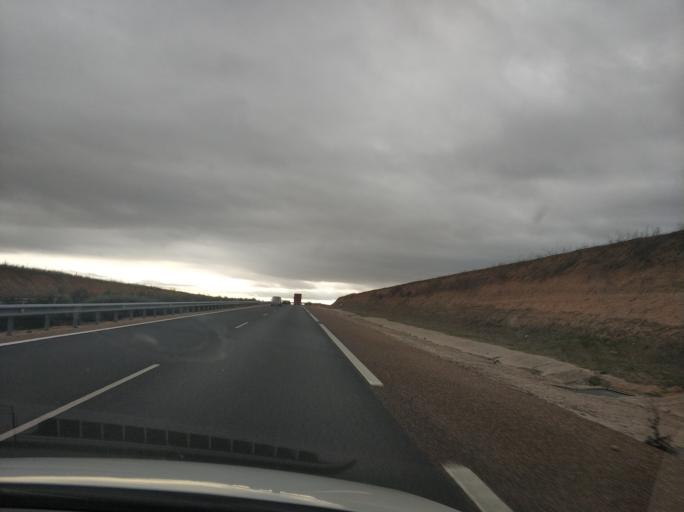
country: ES
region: Castille and Leon
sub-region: Provincia de Valladolid
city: Pollos
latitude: 41.4314
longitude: -5.1028
